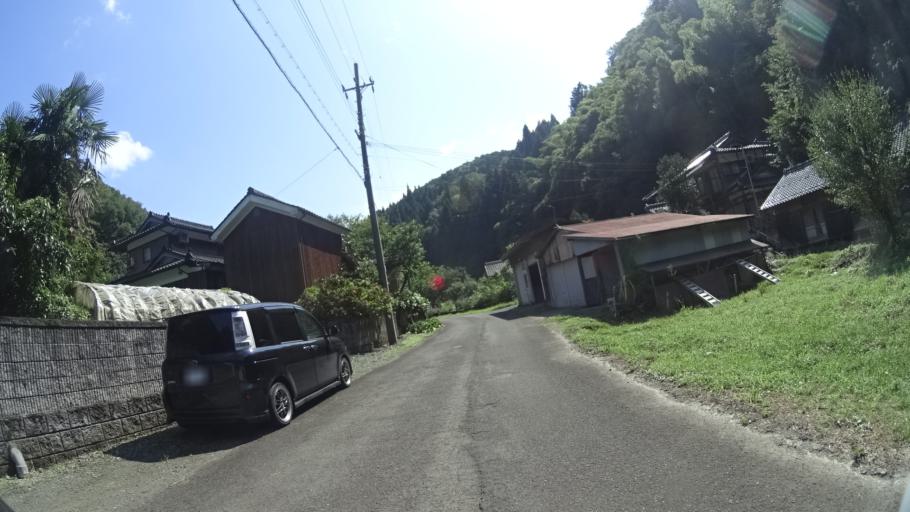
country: JP
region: Kyoto
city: Maizuru
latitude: 35.4161
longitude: 135.3019
